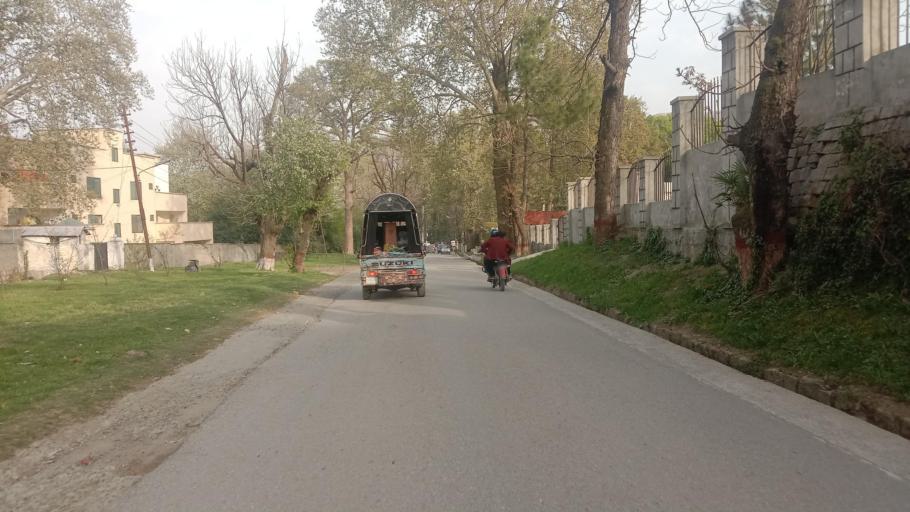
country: PK
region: Khyber Pakhtunkhwa
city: Abbottabad
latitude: 34.1517
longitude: 73.2138
